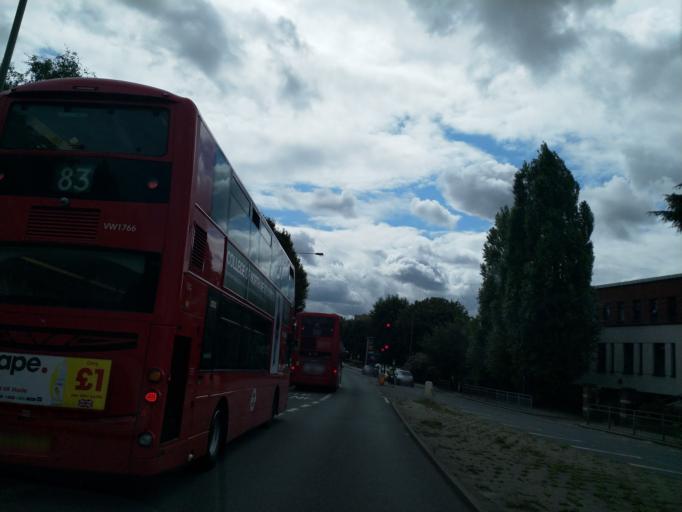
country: GB
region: England
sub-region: Greater London
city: Hendon
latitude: 51.5822
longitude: -0.2453
